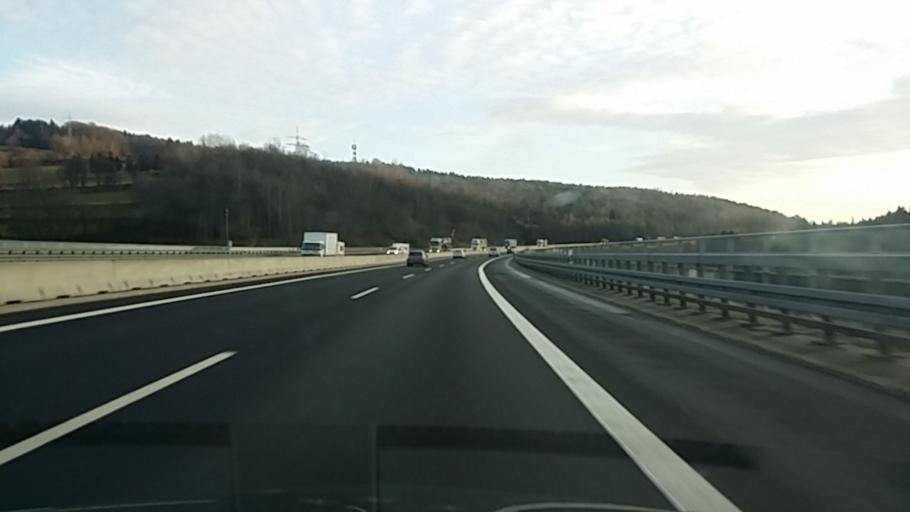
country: DE
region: Bavaria
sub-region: Regierungsbezirk Unterfranken
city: Riedenberg
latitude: 50.3149
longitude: 9.8456
